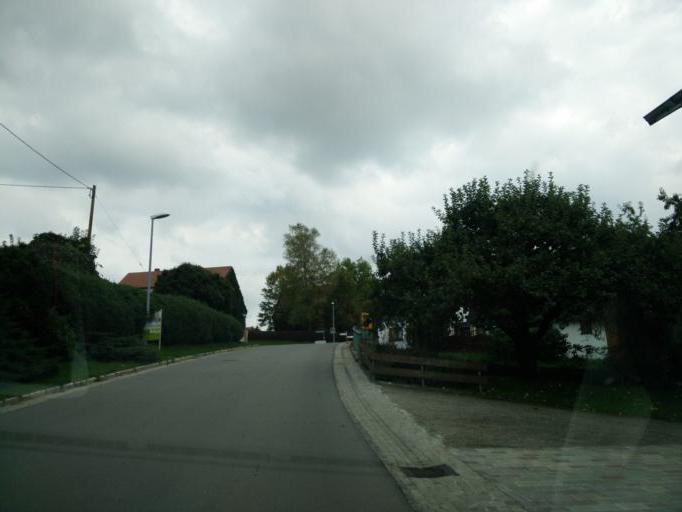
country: DE
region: Baden-Wuerttemberg
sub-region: Tuebingen Region
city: Bad Wurzach
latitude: 47.9402
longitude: 9.9326
